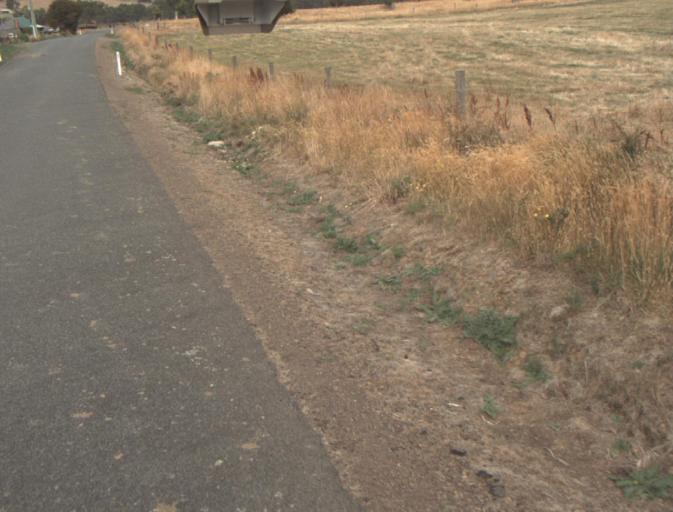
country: AU
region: Tasmania
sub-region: Dorset
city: Scottsdale
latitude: -41.4665
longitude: 147.5868
